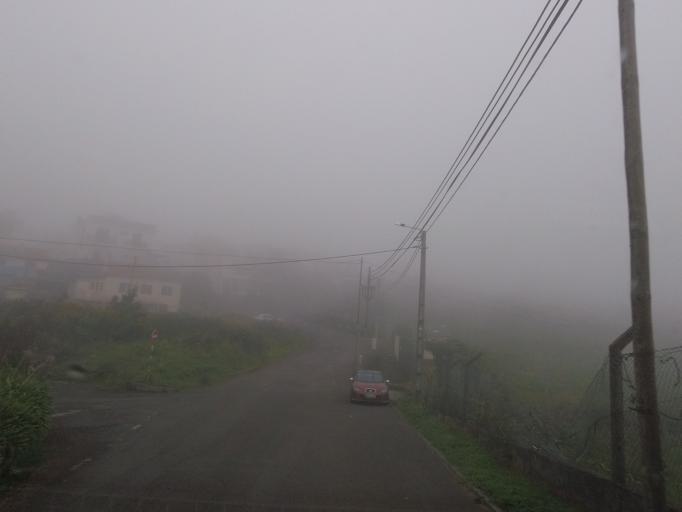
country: PT
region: Madeira
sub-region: Santa Cruz
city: Santa Cruz
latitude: 32.7240
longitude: -16.8209
